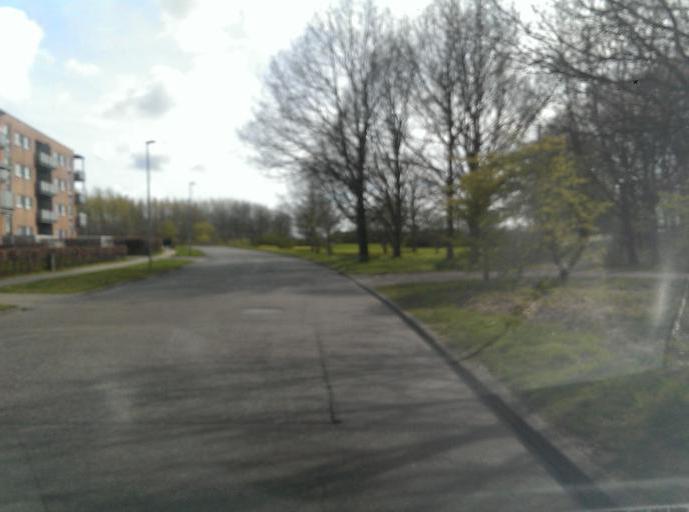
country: DK
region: South Denmark
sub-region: Esbjerg Kommune
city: Esbjerg
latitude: 55.4641
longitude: 8.4705
